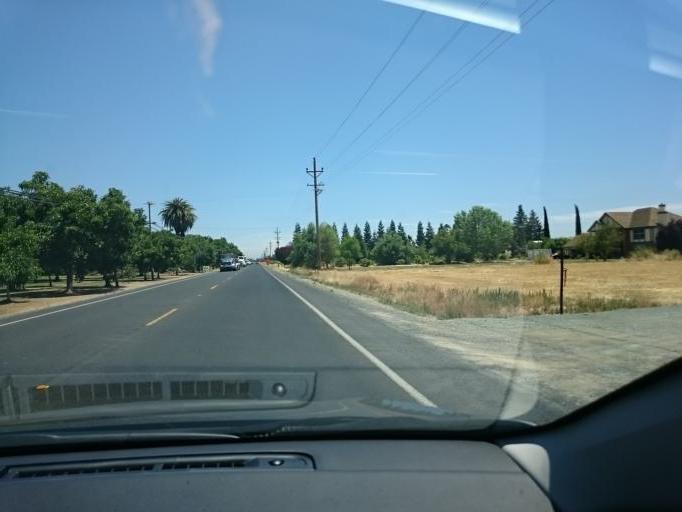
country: US
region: California
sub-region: San Joaquin County
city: Lockeford
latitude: 38.1896
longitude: -121.2043
